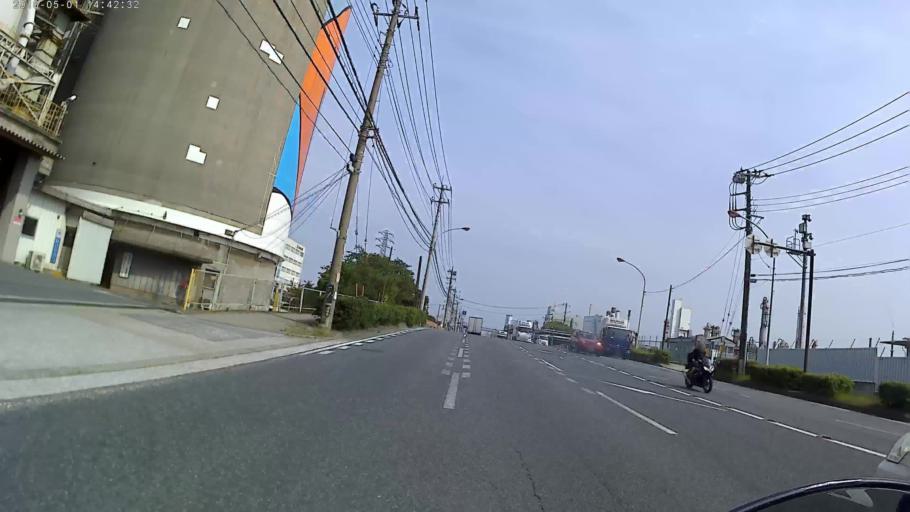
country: JP
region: Kanagawa
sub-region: Kawasaki-shi
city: Kawasaki
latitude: 35.5241
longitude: 139.7515
